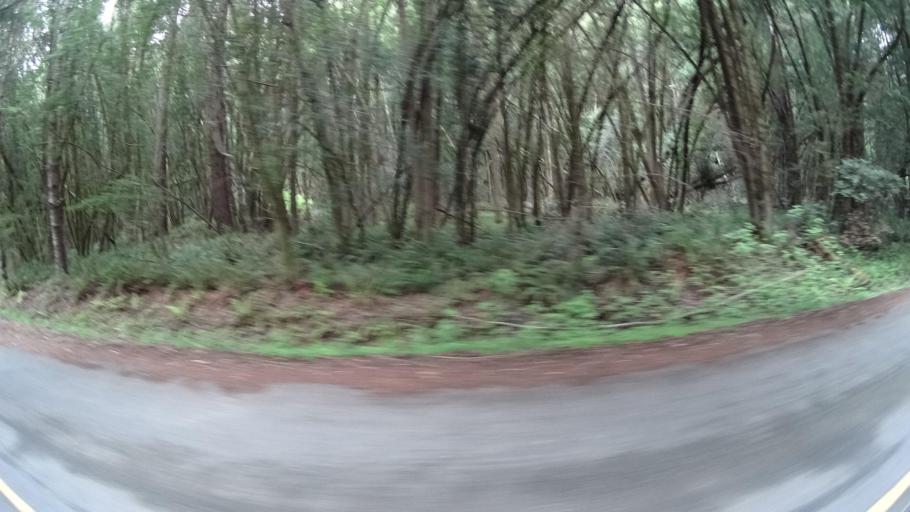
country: US
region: California
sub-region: Humboldt County
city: Blue Lake
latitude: 40.9626
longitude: -123.8400
